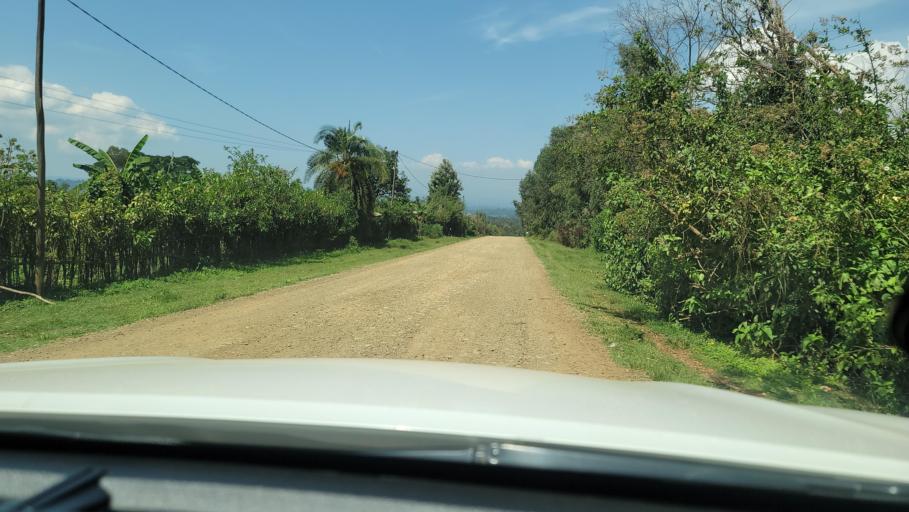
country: ET
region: Oromiya
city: Agaro
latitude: 7.7943
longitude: 36.4467
